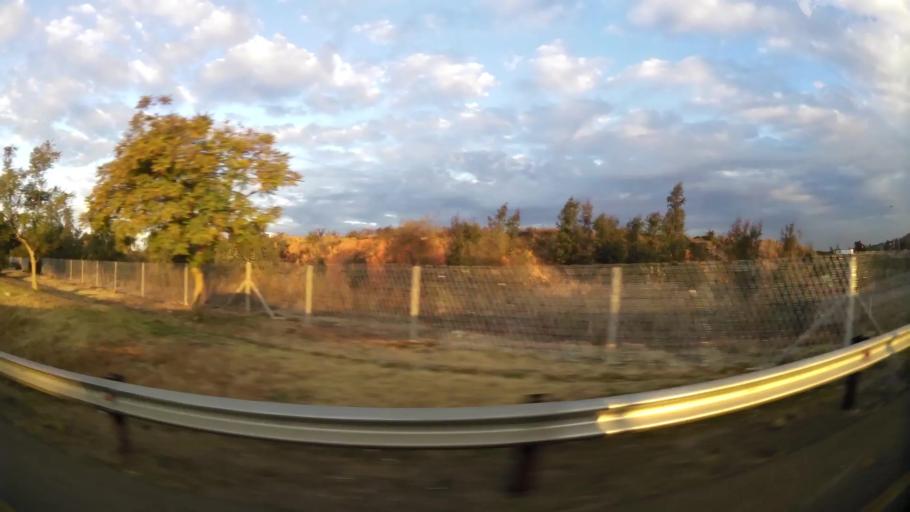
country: ZA
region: Gauteng
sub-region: City of Tshwane Metropolitan Municipality
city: Pretoria
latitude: -25.7410
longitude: 28.2670
